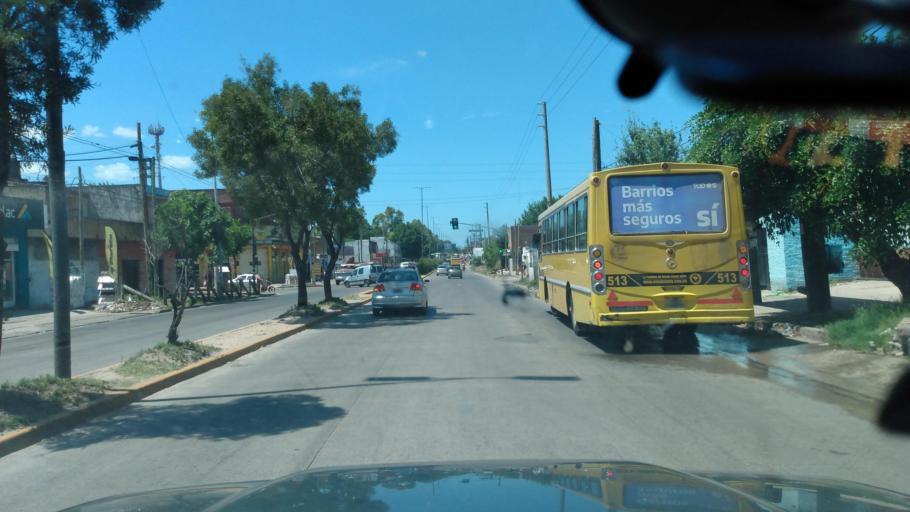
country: AR
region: Buenos Aires
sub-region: Partido de Merlo
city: Merlo
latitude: -34.5667
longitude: -58.7403
